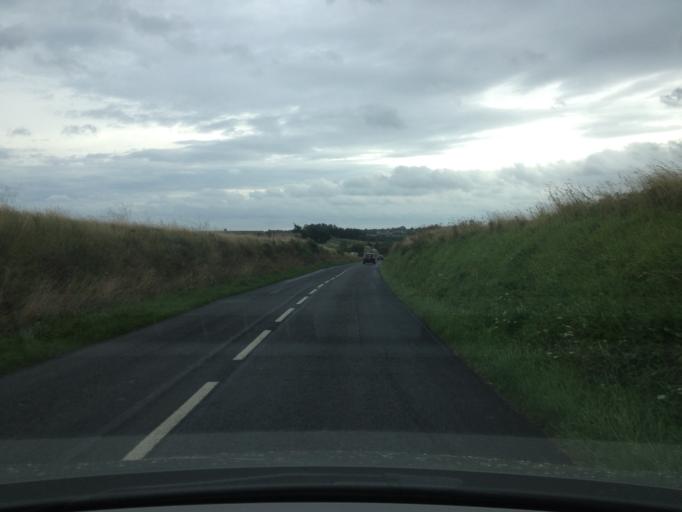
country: FR
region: Lower Normandy
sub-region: Departement du Calvados
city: Grandcamp-Maisy
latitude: 49.3889
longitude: -1.0249
